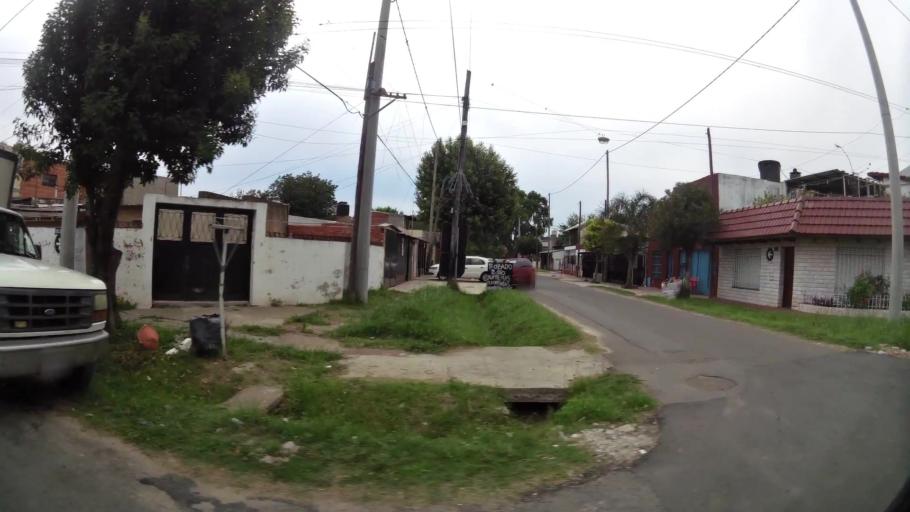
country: AR
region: Santa Fe
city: Granadero Baigorria
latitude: -32.8864
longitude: -60.7058
